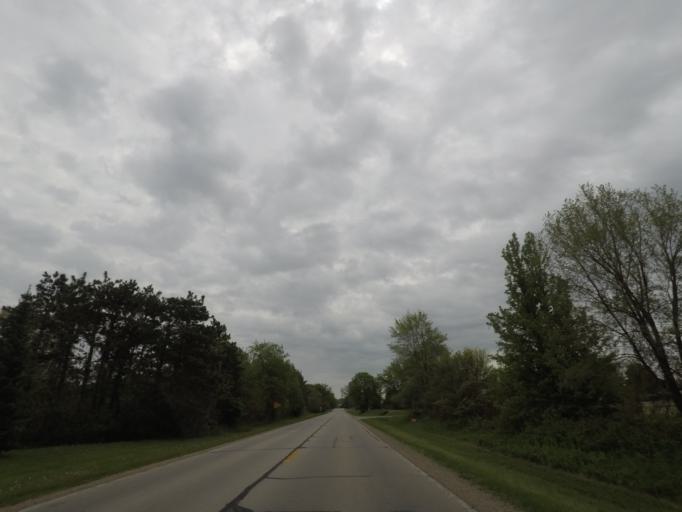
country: US
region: Illinois
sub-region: Winnebago County
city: Roscoe
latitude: 42.4040
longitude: -88.9798
